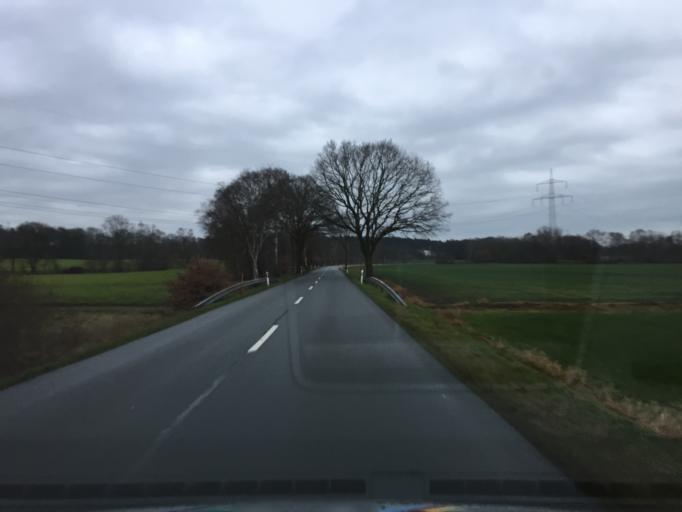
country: DE
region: Lower Saxony
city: Pennigsehl
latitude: 52.6239
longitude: 8.9957
